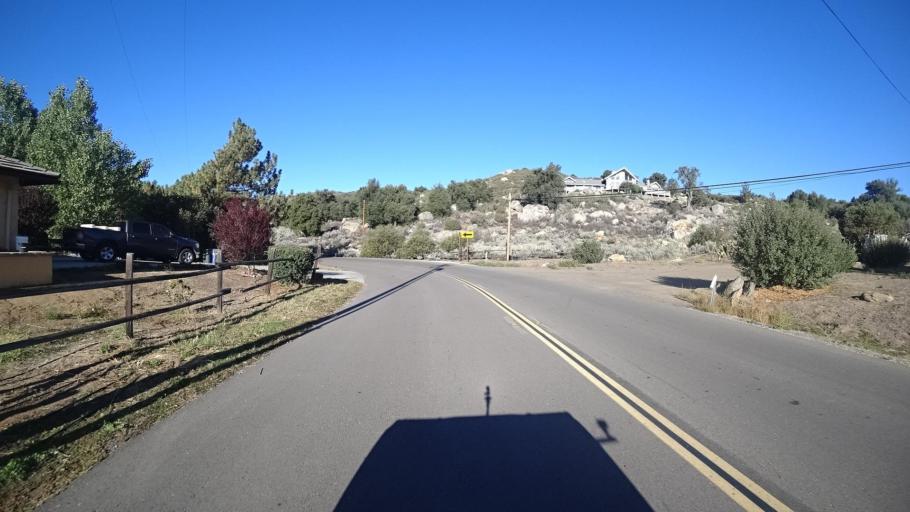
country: US
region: California
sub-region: San Diego County
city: Pine Valley
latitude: 32.8383
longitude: -116.5340
